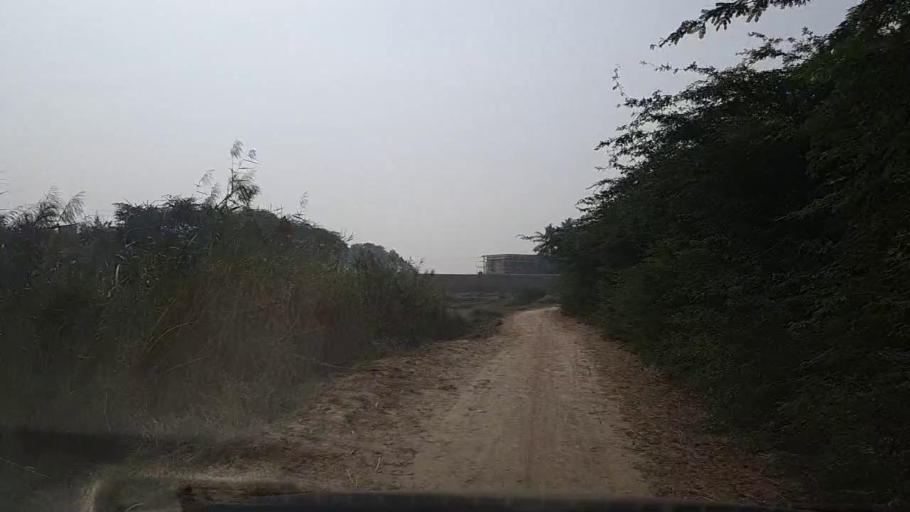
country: PK
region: Sindh
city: Mirpur Sakro
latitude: 24.5525
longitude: 67.8395
